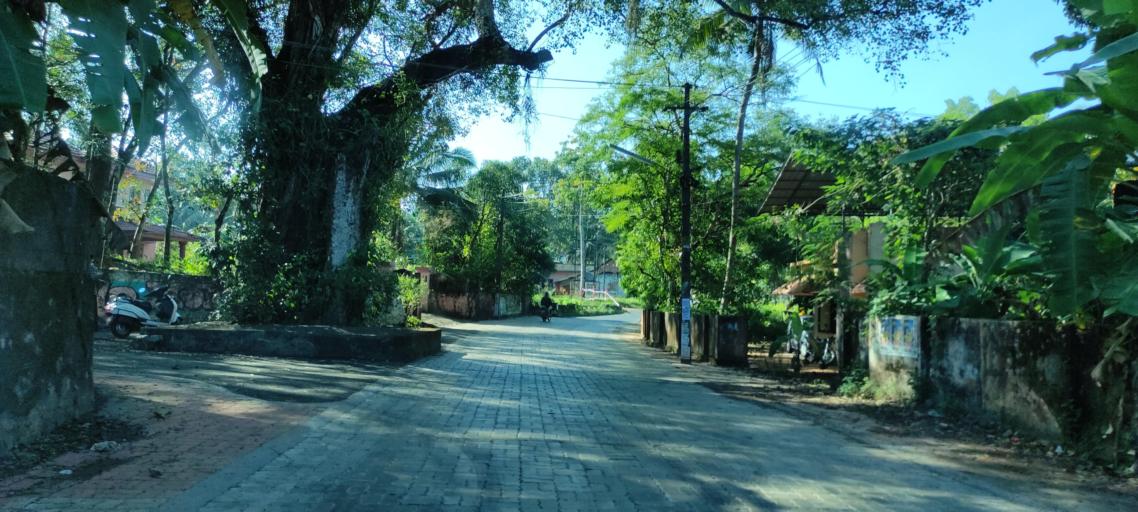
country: IN
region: Kerala
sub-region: Pattanamtitta
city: Adur
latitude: 9.1563
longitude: 76.7151
